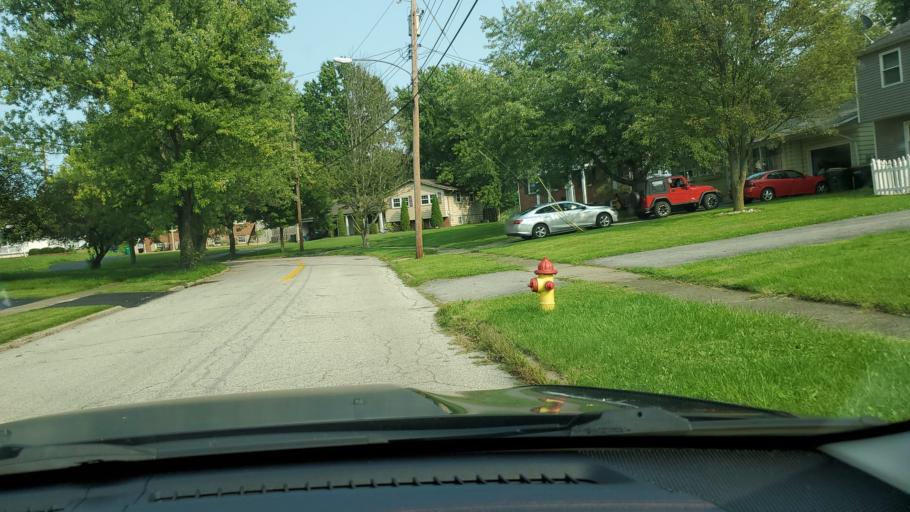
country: US
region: Ohio
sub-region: Mahoning County
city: Poland
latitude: 41.0362
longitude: -80.6230
